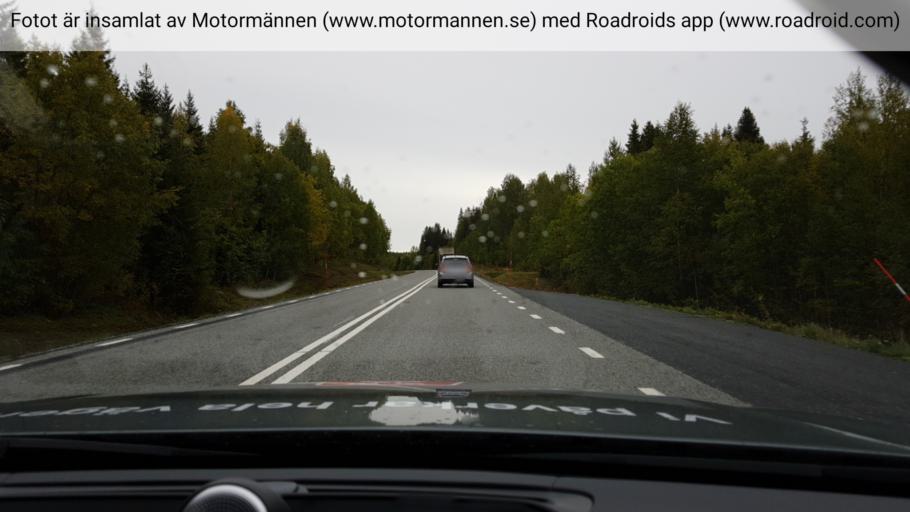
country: SE
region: Jaemtland
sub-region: Stroemsunds Kommun
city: Stroemsund
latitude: 64.1037
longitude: 15.5902
